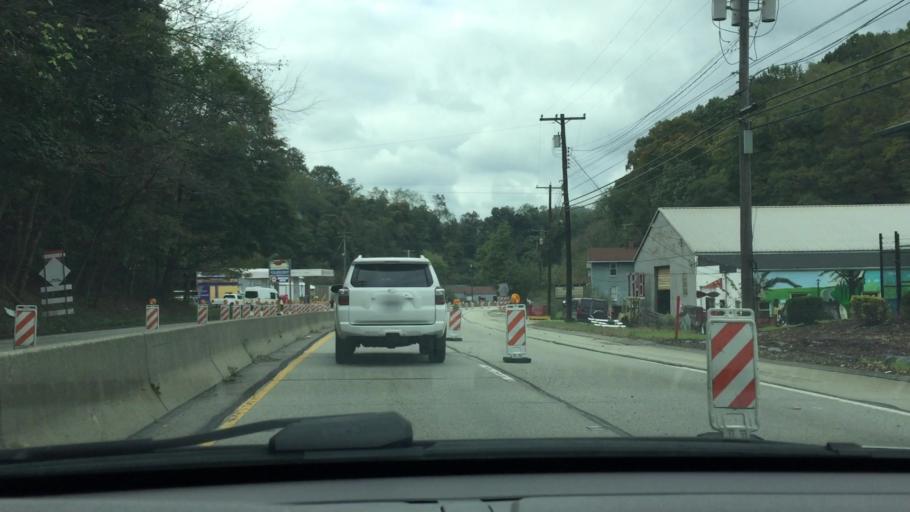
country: US
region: Pennsylvania
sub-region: Allegheny County
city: Elizabeth
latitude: 40.2668
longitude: -79.8817
